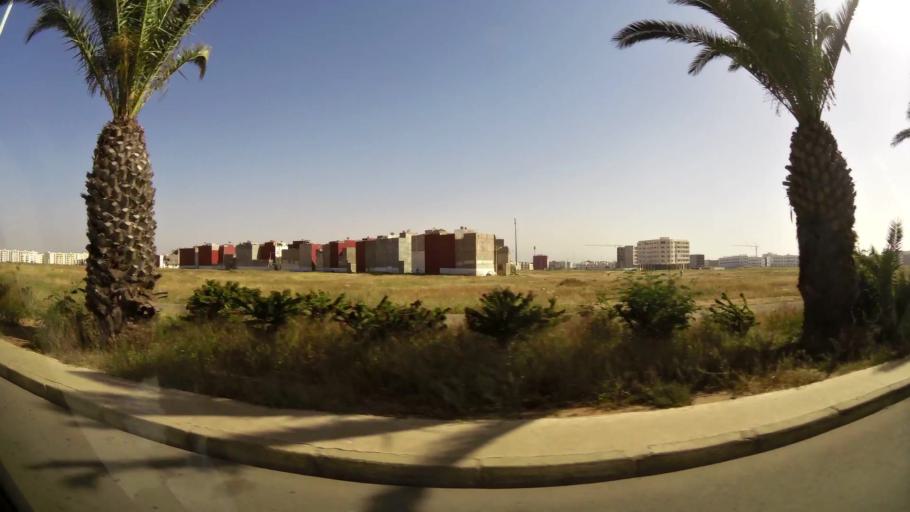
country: MA
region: Oued ed Dahab-Lagouira
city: Dakhla
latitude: 30.4036
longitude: -9.5633
